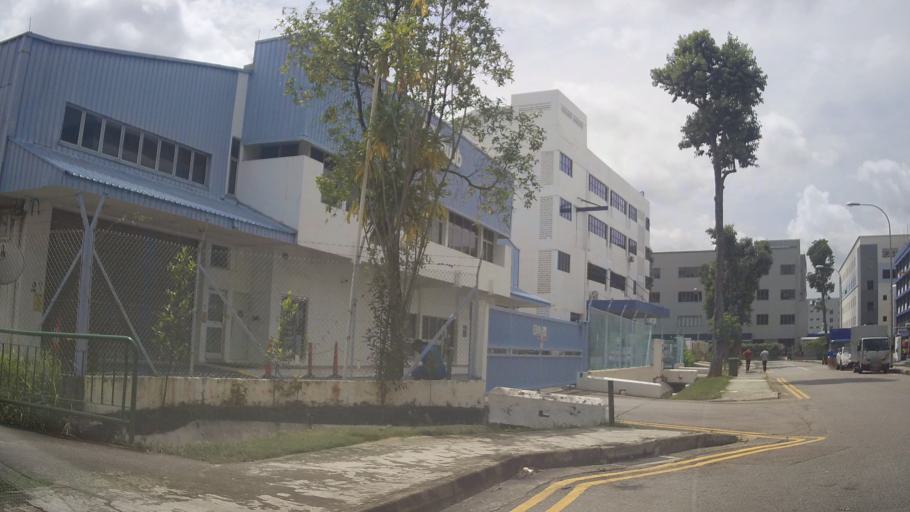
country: SG
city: Singapore
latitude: 1.3189
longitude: 103.8664
